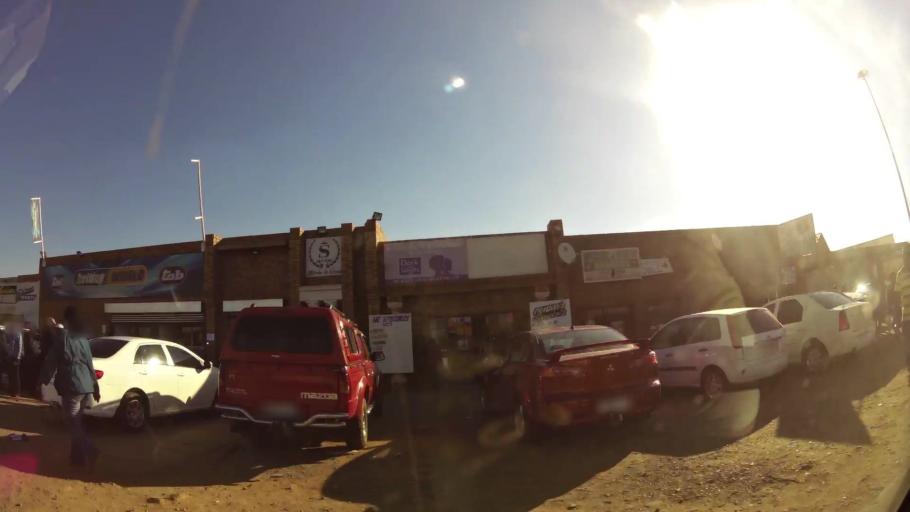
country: ZA
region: Gauteng
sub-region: City of Tshwane Metropolitan Municipality
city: Cullinan
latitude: -25.7104
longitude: 28.3896
